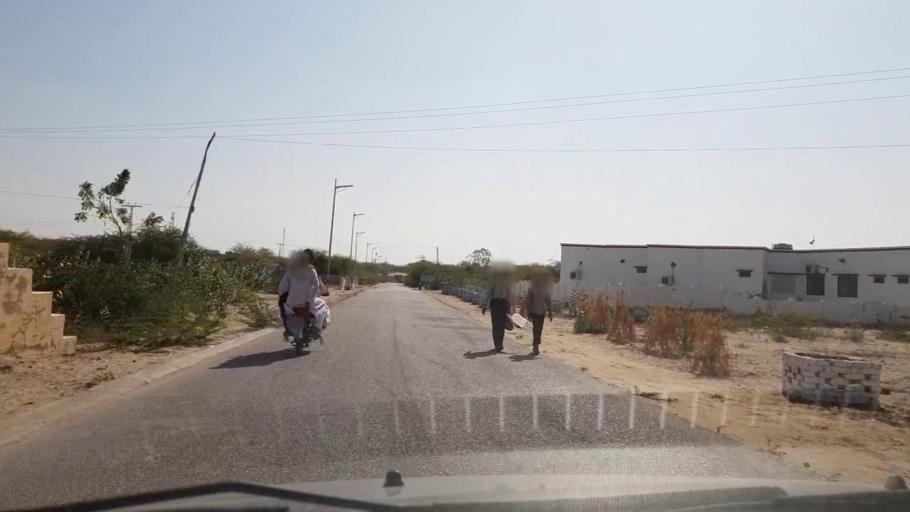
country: PK
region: Sindh
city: Diplo
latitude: 24.4762
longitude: 69.5806
